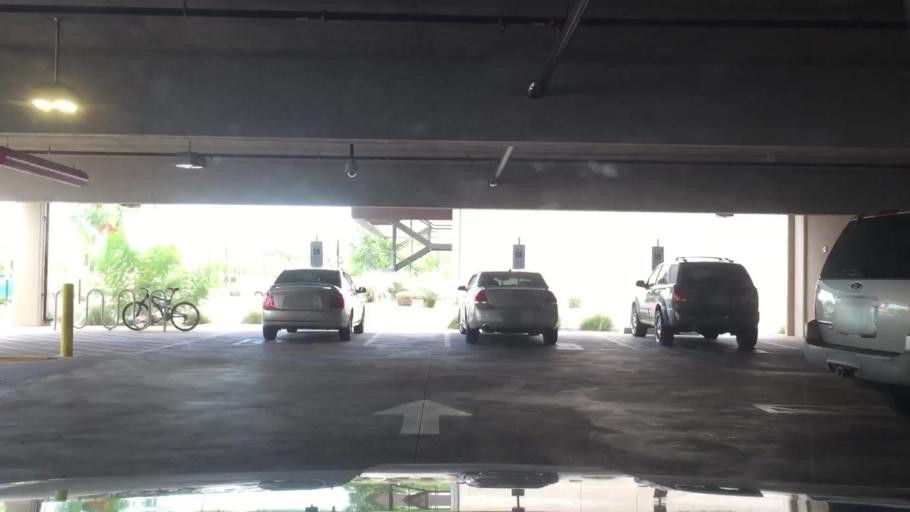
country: US
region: Arizona
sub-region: Maricopa County
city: Tolleson
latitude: 33.4778
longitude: -112.2590
